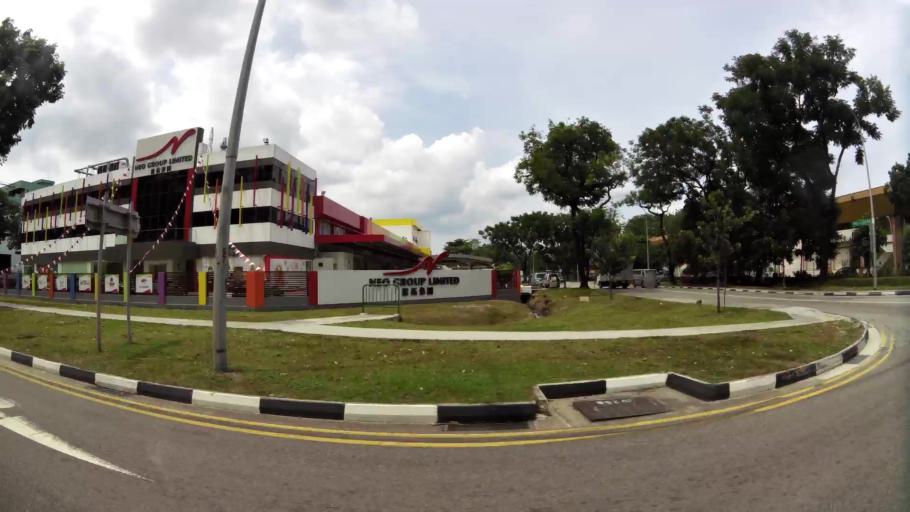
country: MY
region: Johor
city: Johor Bahru
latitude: 1.3327
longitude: 103.7084
